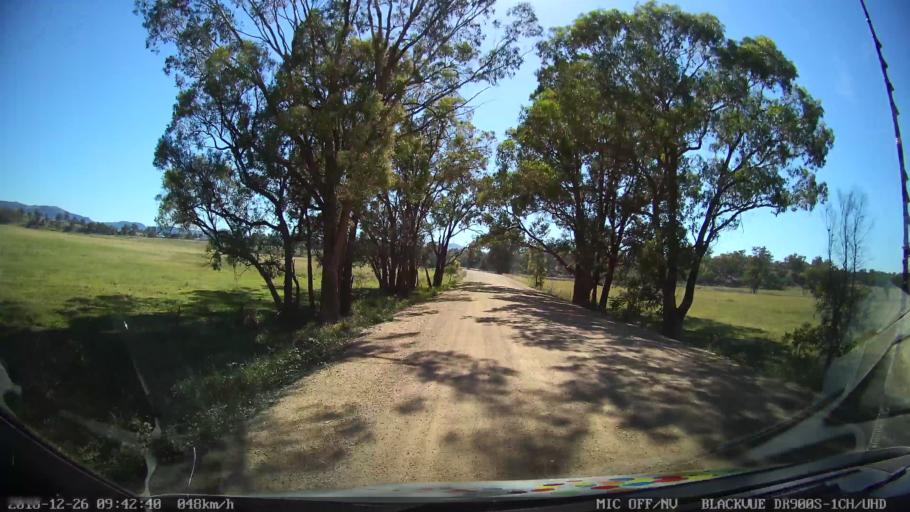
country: AU
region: New South Wales
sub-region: Mid-Western Regional
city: Kandos
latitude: -32.9551
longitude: 150.0834
